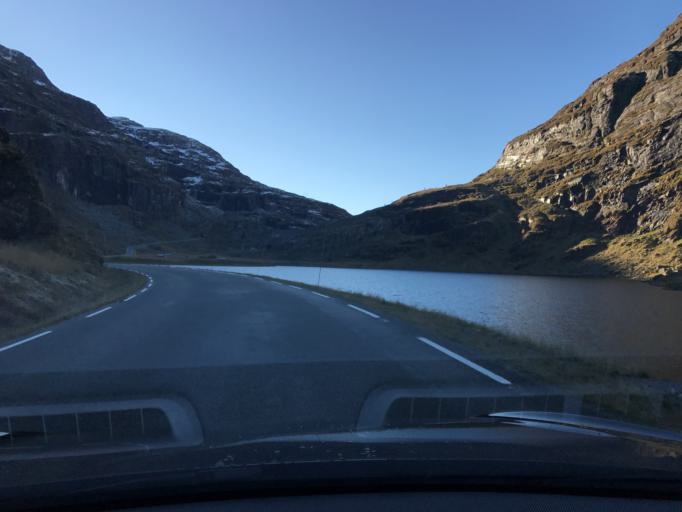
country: NO
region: Sogn og Fjordane
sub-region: Laerdal
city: Laerdalsoyri
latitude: 60.8074
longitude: 7.5593
